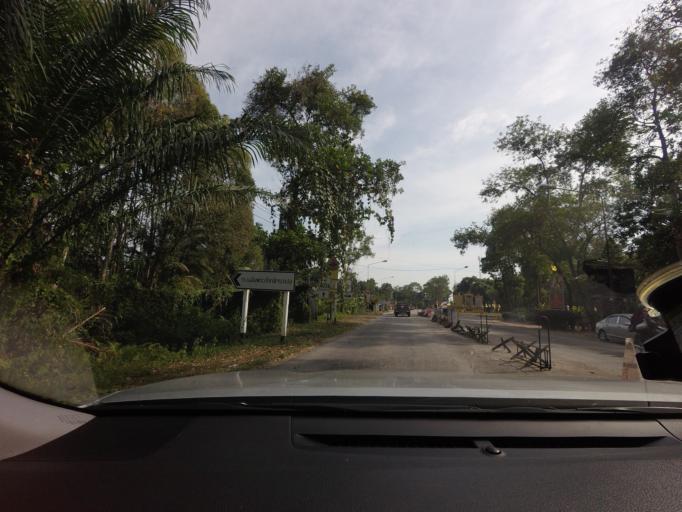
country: TH
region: Narathiwat
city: Ra-ngae
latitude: 6.3260
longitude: 101.7887
